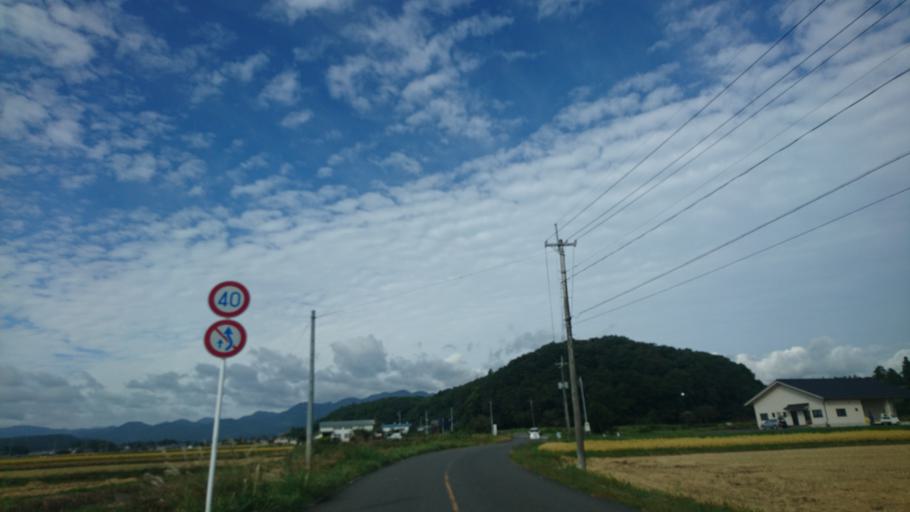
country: JP
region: Fukushima
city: Sukagawa
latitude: 37.3286
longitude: 140.2833
